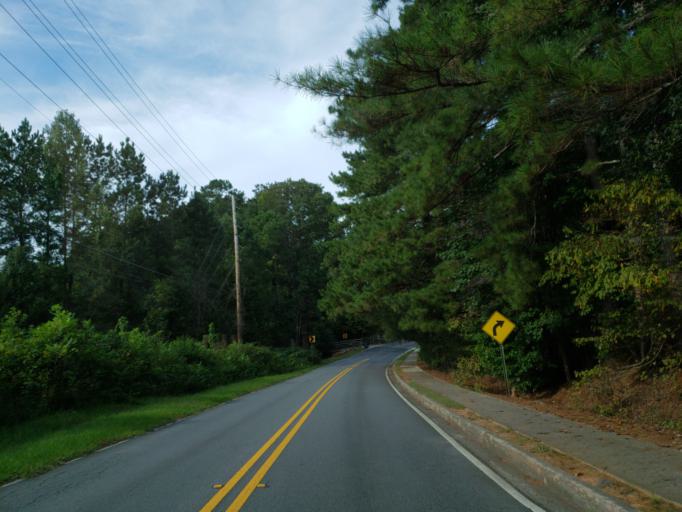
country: US
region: Georgia
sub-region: Cherokee County
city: Woodstock
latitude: 34.0587
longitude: -84.4978
